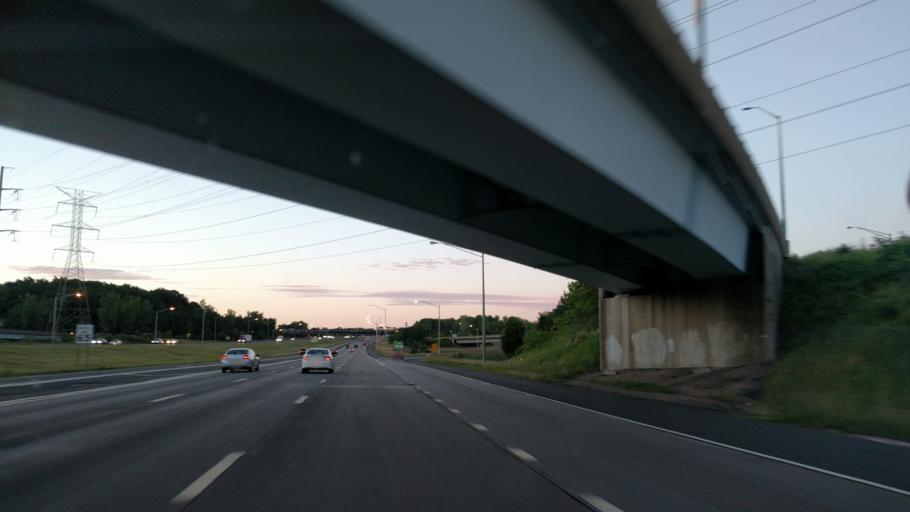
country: US
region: Connecticut
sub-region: Hartford County
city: Manchester
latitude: 41.7881
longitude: -72.5643
